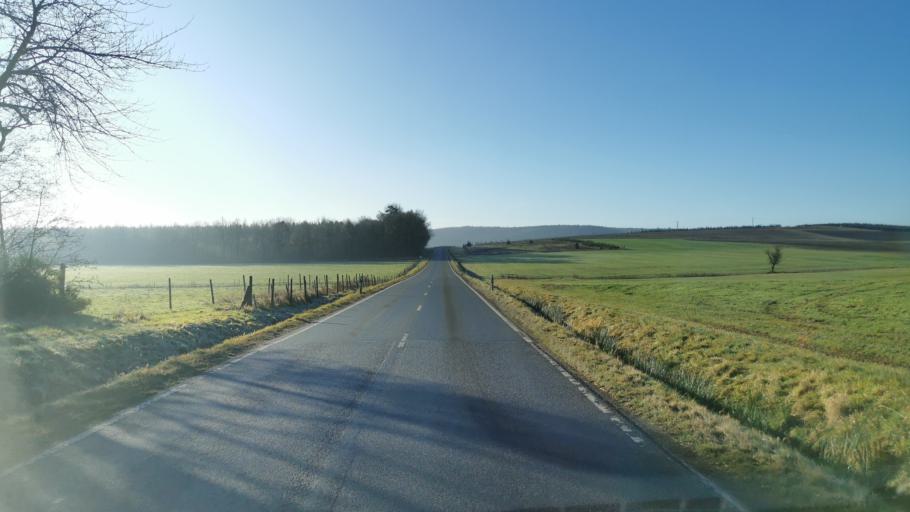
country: DE
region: Rheinland-Pfalz
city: Salm
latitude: 50.1479
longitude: 6.7019
